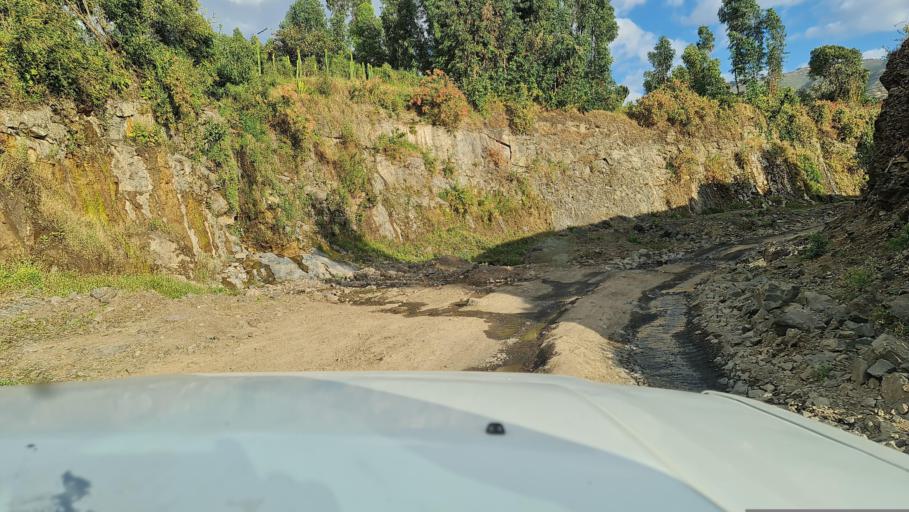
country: ET
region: Amhara
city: Debark'
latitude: 13.0410
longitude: 38.0381
